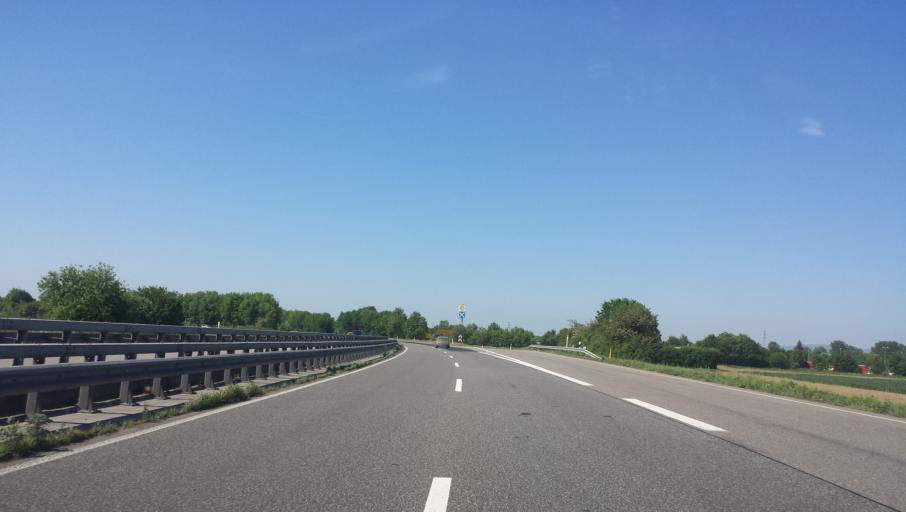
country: DE
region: Rheinland-Pfalz
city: Harthausen
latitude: 49.2775
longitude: 8.3472
